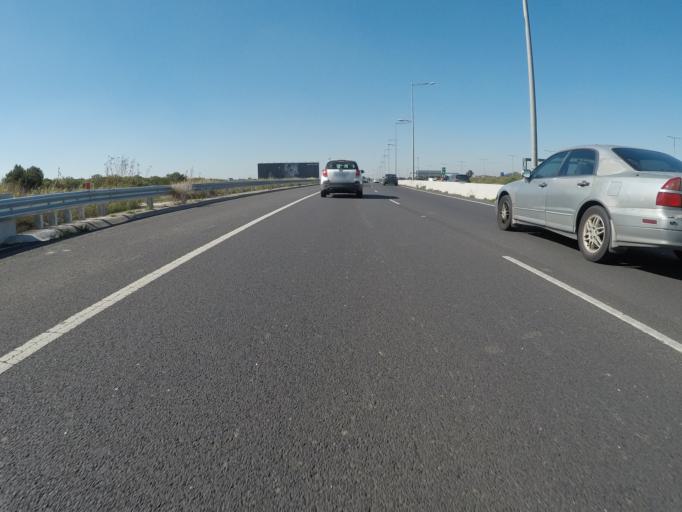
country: AU
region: Victoria
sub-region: Moonee Valley
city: Niddrie
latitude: -37.7337
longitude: 144.8956
